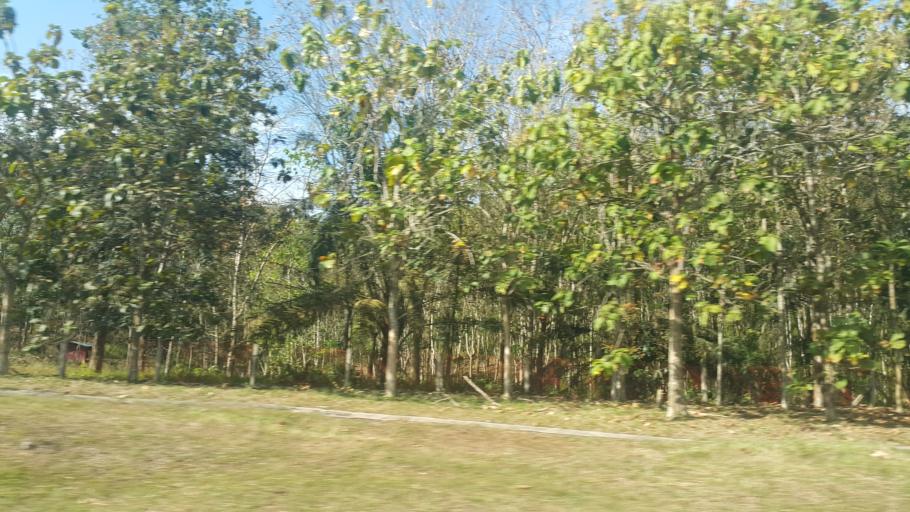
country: MY
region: Johor
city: Kelapa Sawit
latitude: 1.6782
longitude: 103.4794
